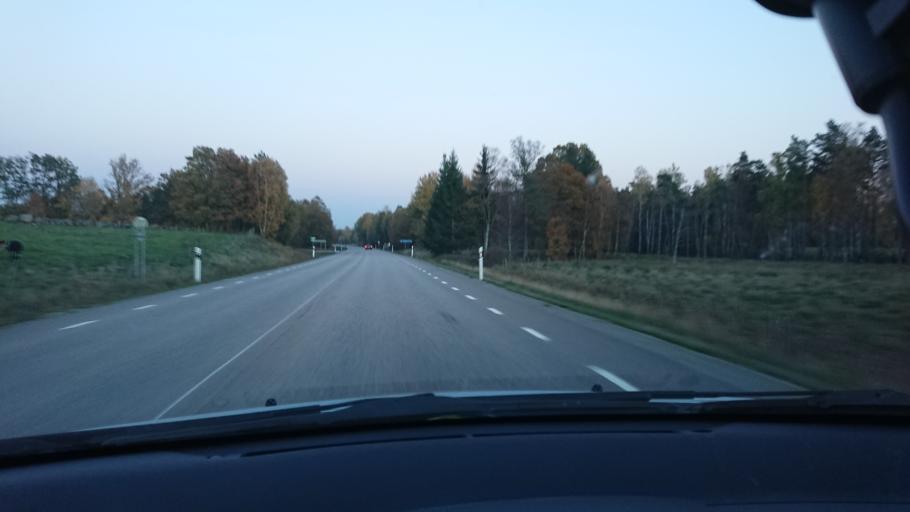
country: SE
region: Kronoberg
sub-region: Markaryds Kommun
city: Stromsnasbruk
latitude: 56.7555
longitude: 13.7220
